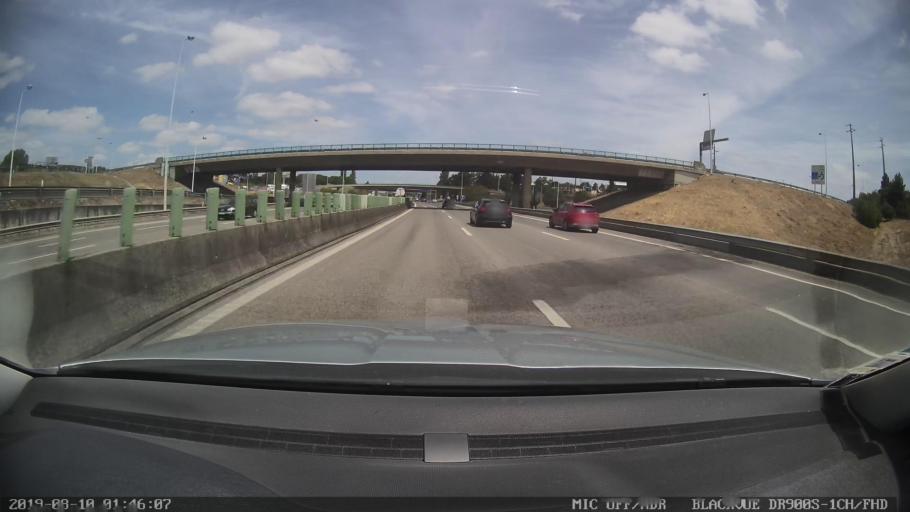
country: PT
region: Lisbon
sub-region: Vila Franca de Xira
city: Vialonga
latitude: 38.8923
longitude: -9.0541
